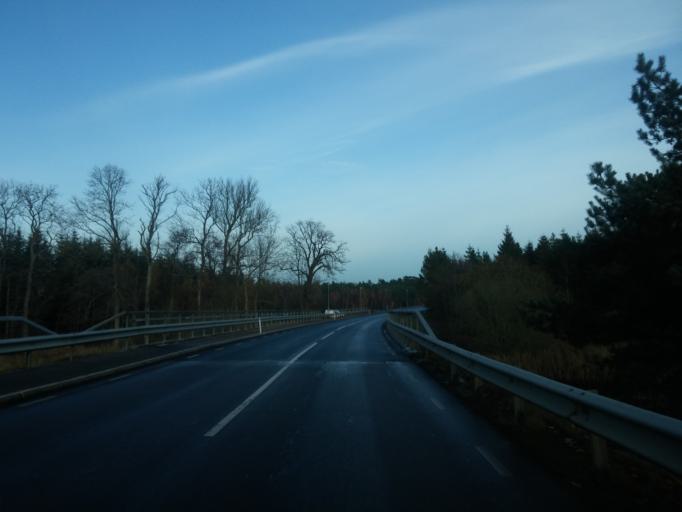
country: SE
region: Skane
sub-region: Angelholms Kommun
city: Strovelstorp
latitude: 56.2140
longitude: 12.7957
